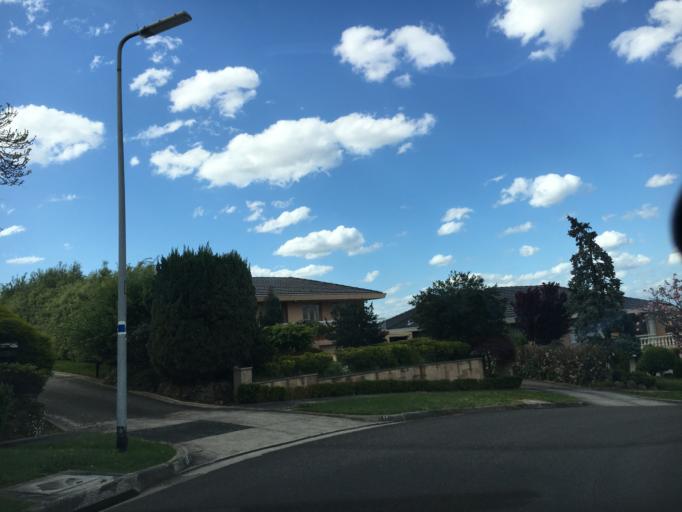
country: AU
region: Victoria
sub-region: Whitehorse
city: Vermont South
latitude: -37.8874
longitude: 145.1745
